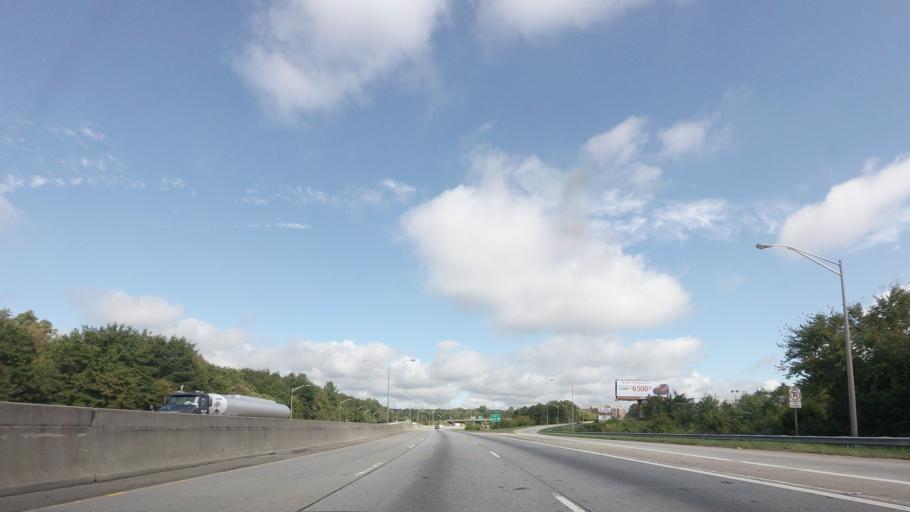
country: US
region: Georgia
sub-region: Bibb County
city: Macon
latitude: 32.8213
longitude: -83.6561
